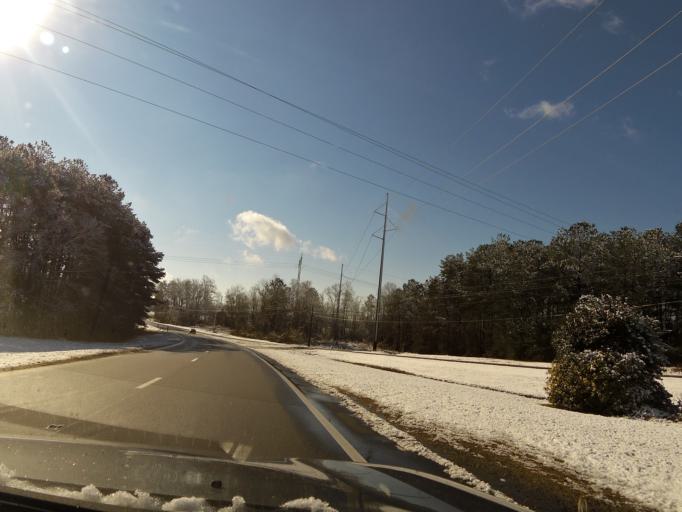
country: US
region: North Carolina
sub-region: Wilson County
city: Elm City
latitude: 35.7833
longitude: -77.8588
